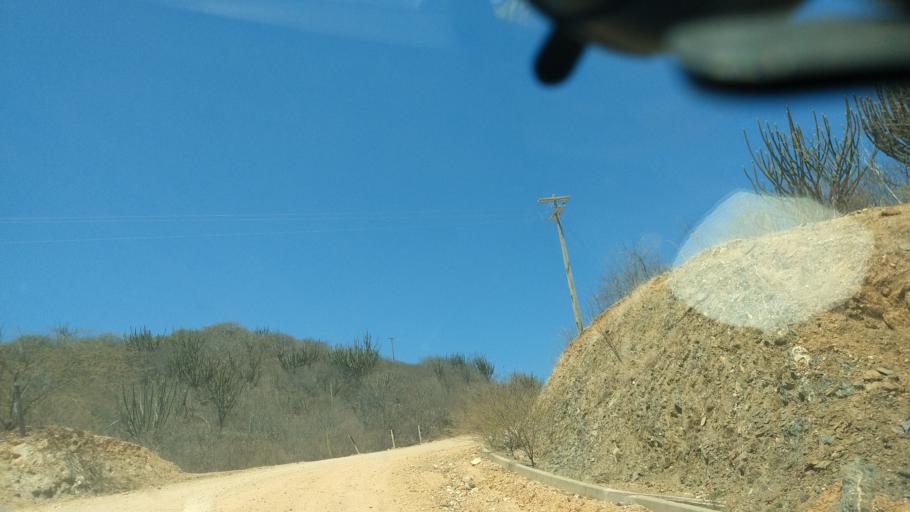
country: BR
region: Rio Grande do Norte
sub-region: Cerro Cora
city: Cerro Cora
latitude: -6.0117
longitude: -36.2782
